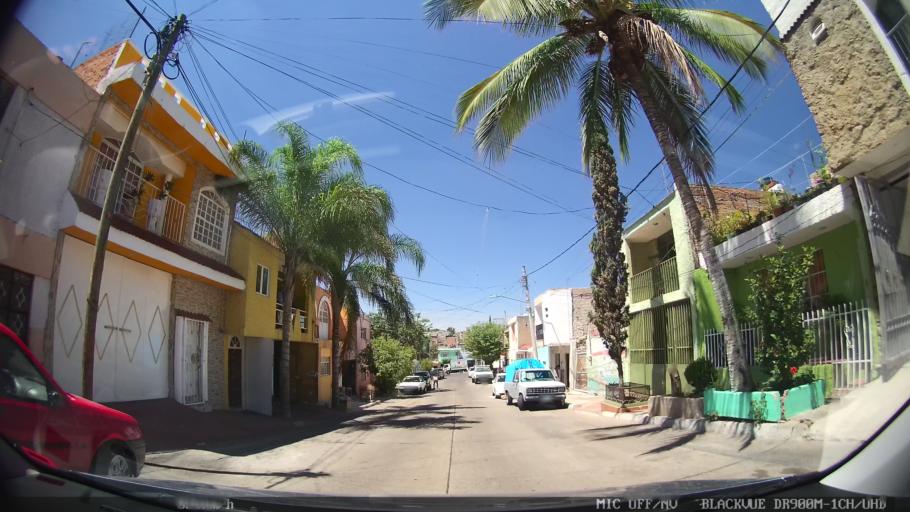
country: MX
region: Jalisco
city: Tlaquepaque
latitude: 20.6954
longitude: -103.2907
